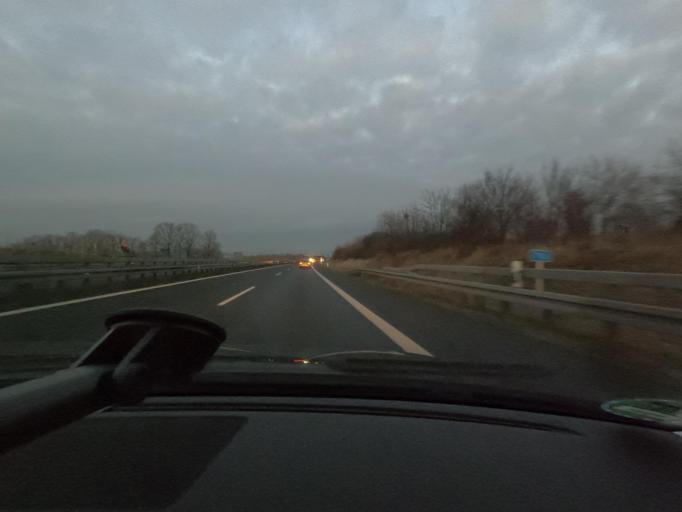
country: DE
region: Bavaria
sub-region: Upper Franconia
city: Bad Staffelstein
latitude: 50.1208
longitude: 11.0231
